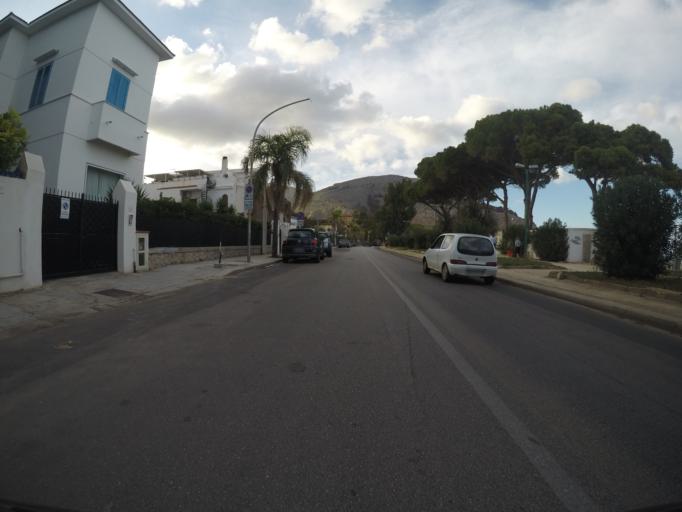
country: IT
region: Sicily
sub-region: Palermo
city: Palermo
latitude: 38.1998
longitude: 13.3282
